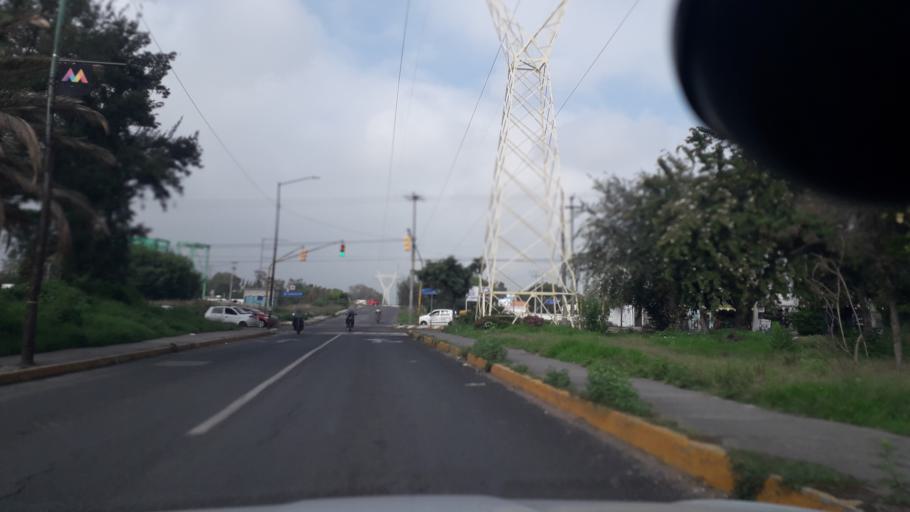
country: MX
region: Mexico
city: Coacalco
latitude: 19.6444
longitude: -99.0902
